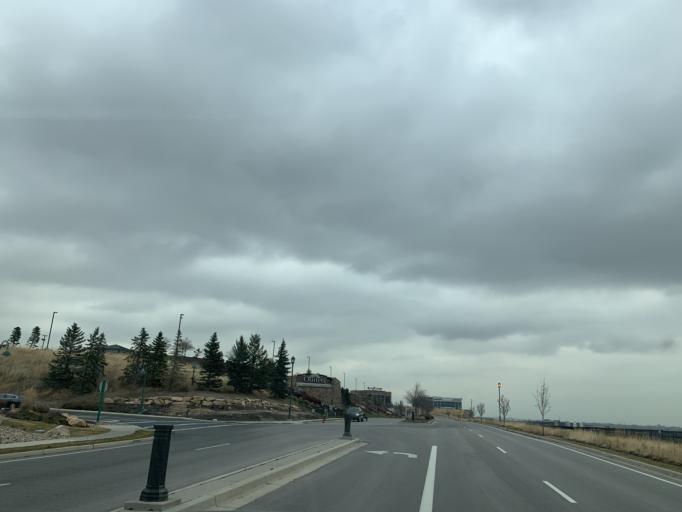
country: US
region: Utah
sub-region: Utah County
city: Lehi
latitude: 40.4353
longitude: -111.8889
